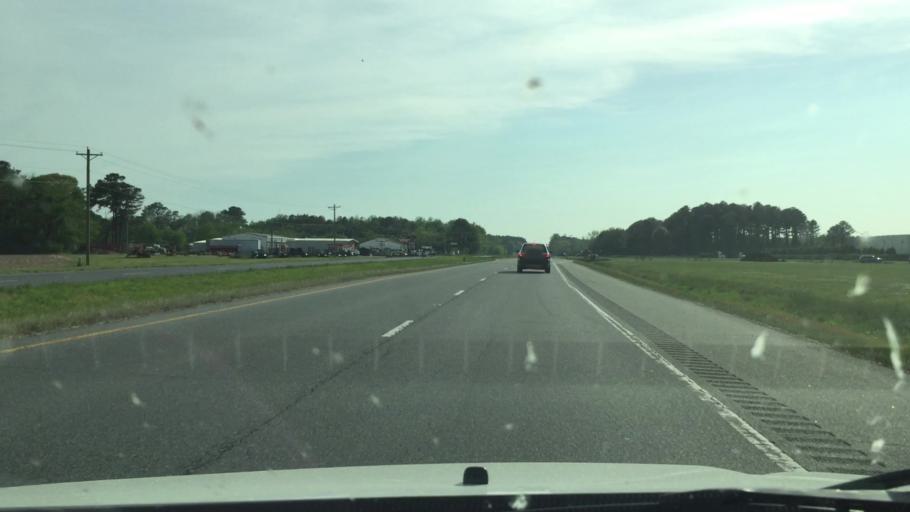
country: US
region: Virginia
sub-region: Accomack County
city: Accomac
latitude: 37.7334
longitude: -75.6529
